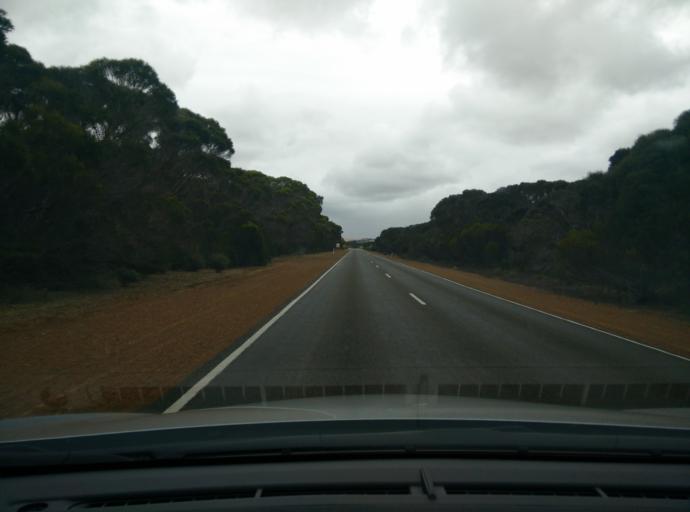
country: AU
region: South Australia
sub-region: Kangaroo Island
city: Kingscote
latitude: -35.7213
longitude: 137.5600
